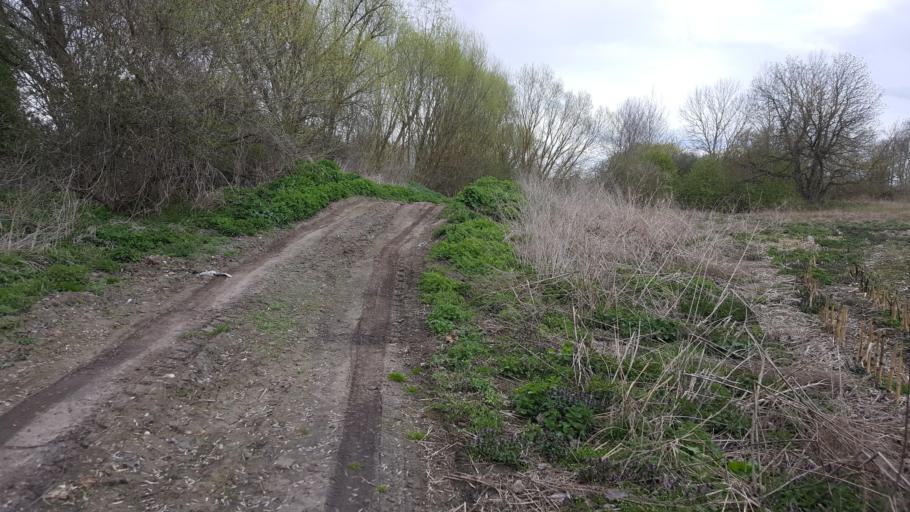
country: BY
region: Brest
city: Kamyanyets
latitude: 52.4072
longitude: 23.7077
